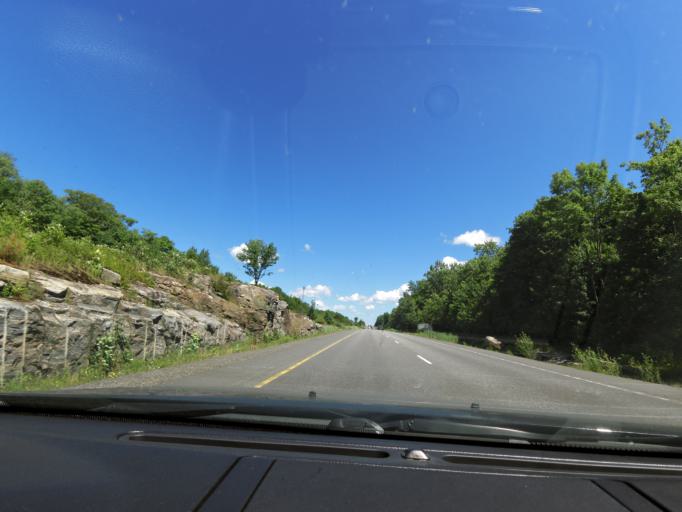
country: CA
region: Ontario
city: Bracebridge
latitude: 45.1467
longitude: -79.3111
